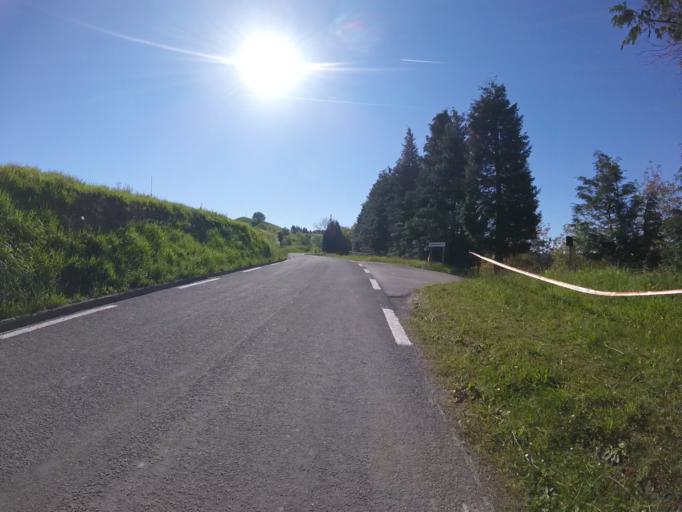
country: ES
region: Basque Country
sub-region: Provincia de Guipuzcoa
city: Aizarnazabal
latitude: 43.2179
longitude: -2.2145
